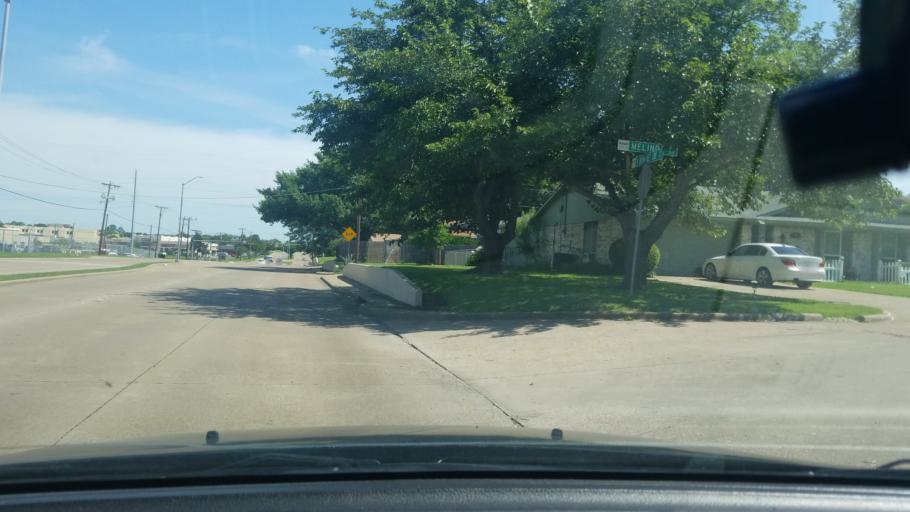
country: US
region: Texas
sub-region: Dallas County
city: Mesquite
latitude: 32.7735
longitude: -96.5970
